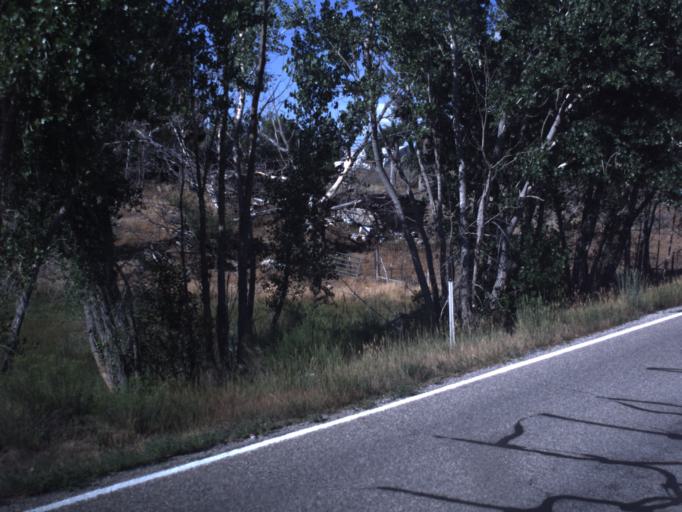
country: US
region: Utah
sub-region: Emery County
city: Huntington
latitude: 39.3481
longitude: -110.8656
